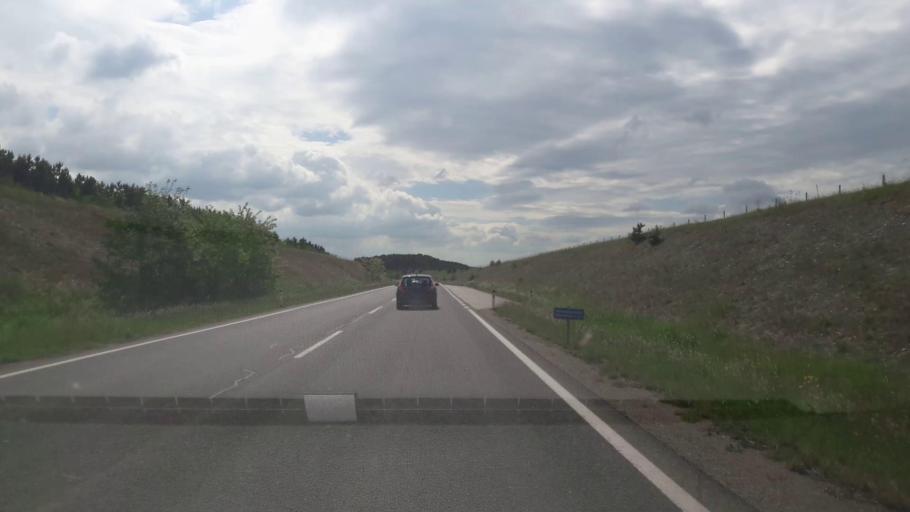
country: AT
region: Lower Austria
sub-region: Politischer Bezirk Wiener Neustadt
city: Theresienfeld
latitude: 47.8505
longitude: 16.2219
